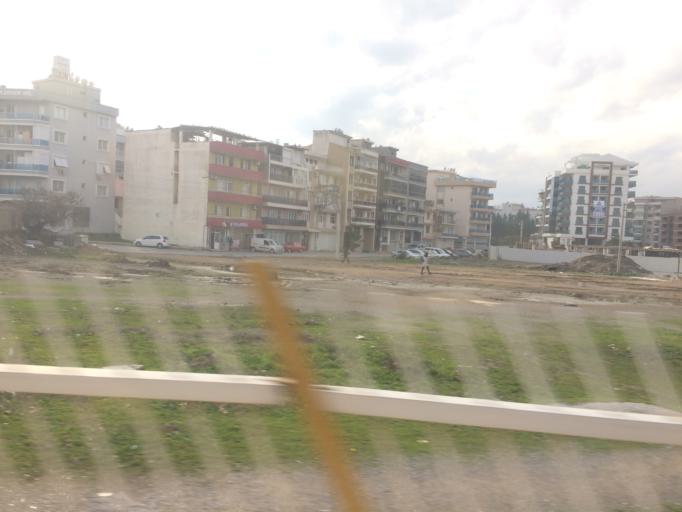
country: TR
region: Izmir
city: Karsiyaka
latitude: 38.4736
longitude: 27.0910
